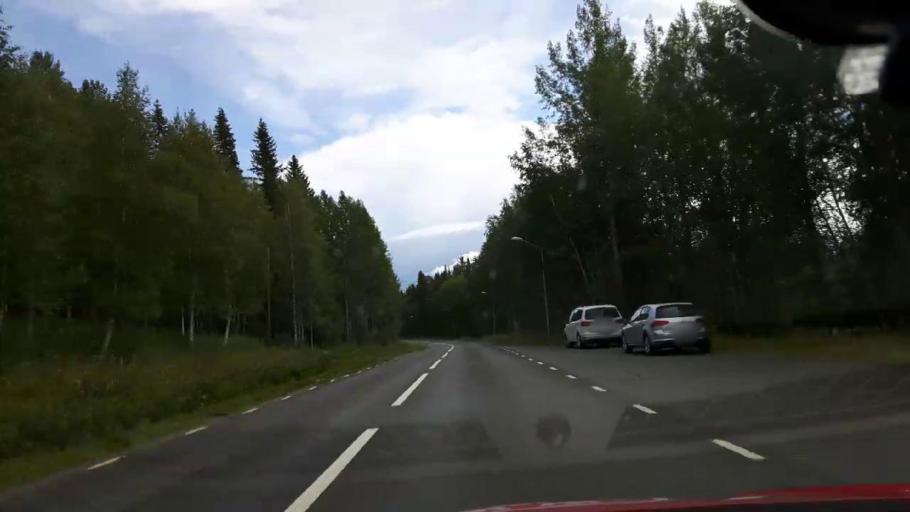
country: SE
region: Jaemtland
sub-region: Stroemsunds Kommun
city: Stroemsund
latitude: 64.3381
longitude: 14.9556
